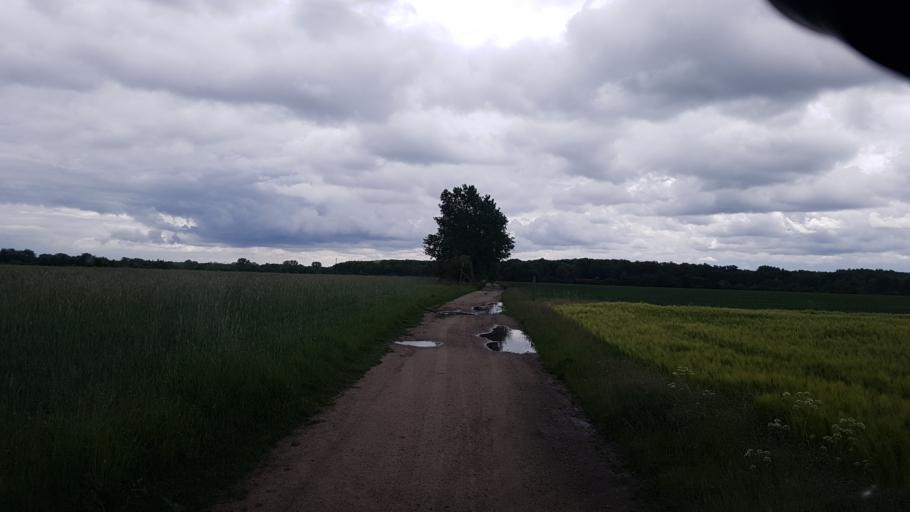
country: DE
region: Brandenburg
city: Doberlug-Kirchhain
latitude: 51.6300
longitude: 13.5397
